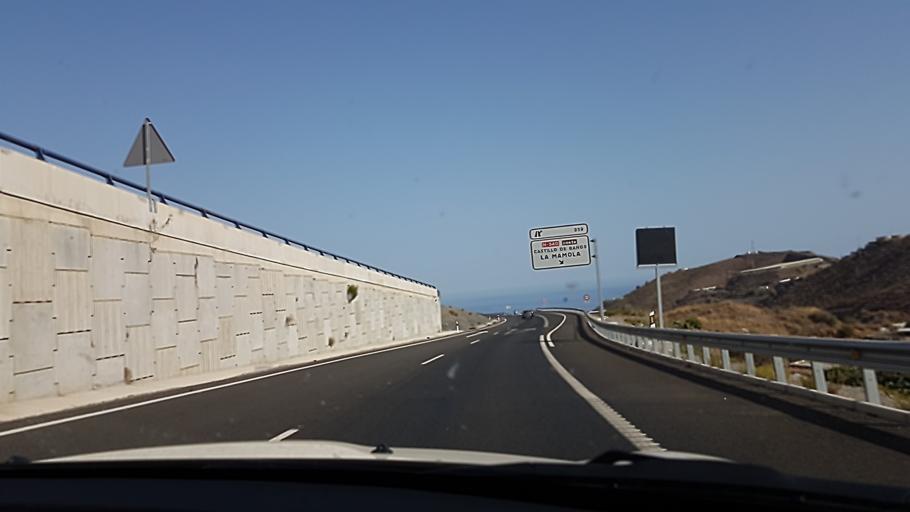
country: ES
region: Andalusia
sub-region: Provincia de Granada
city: Polopos
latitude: 36.7508
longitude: -3.3188
